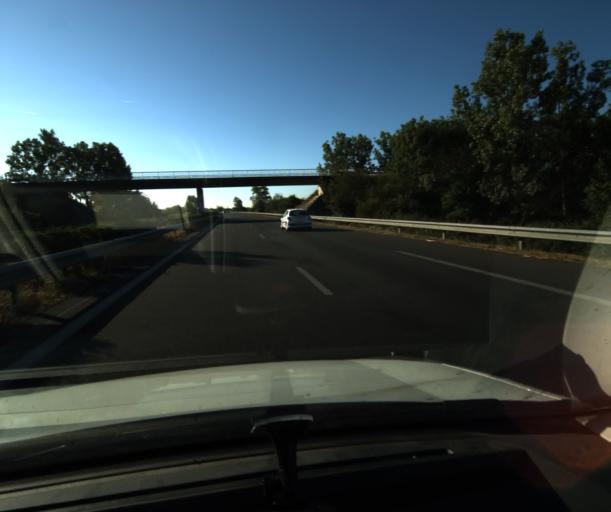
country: FR
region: Midi-Pyrenees
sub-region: Departement du Tarn-et-Garonne
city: Saint-Porquier
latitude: 44.0254
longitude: 1.1687
